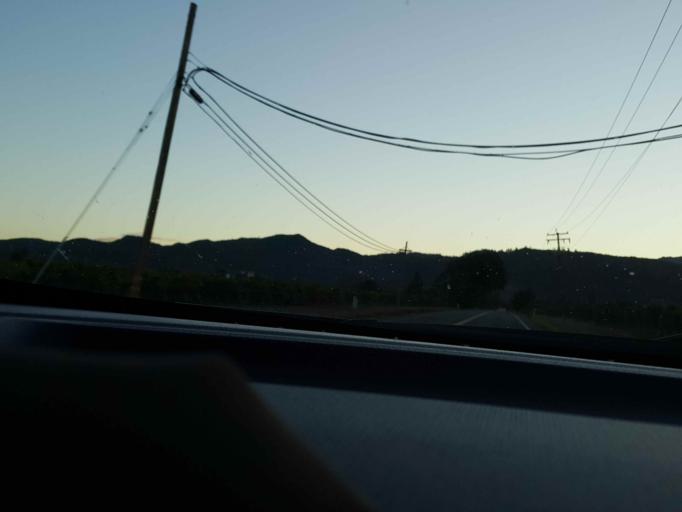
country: US
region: California
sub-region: Napa County
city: Yountville
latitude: 38.4160
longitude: -122.3550
